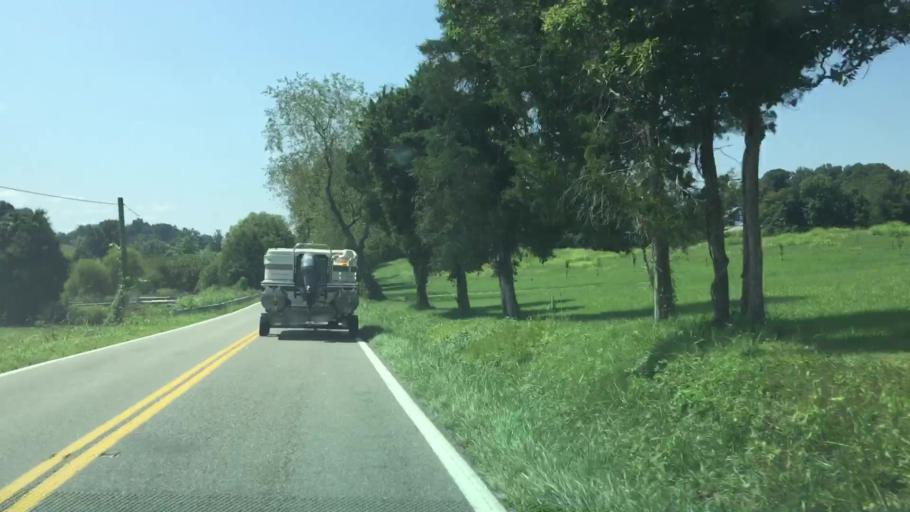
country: US
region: Virginia
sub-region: Washington County
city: Abingdon
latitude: 36.6185
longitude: -82.0161
